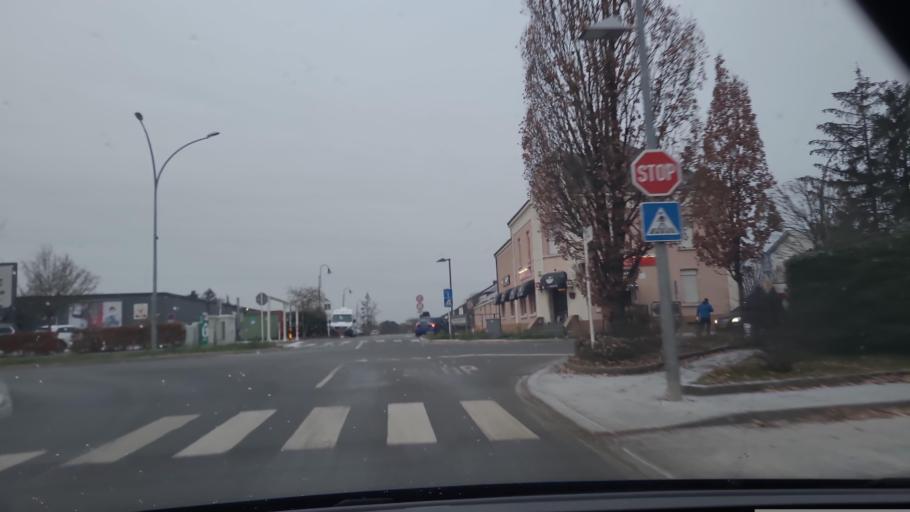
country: LU
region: Luxembourg
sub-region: Canton de Capellen
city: Koerich
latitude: 49.6476
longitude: 5.9560
